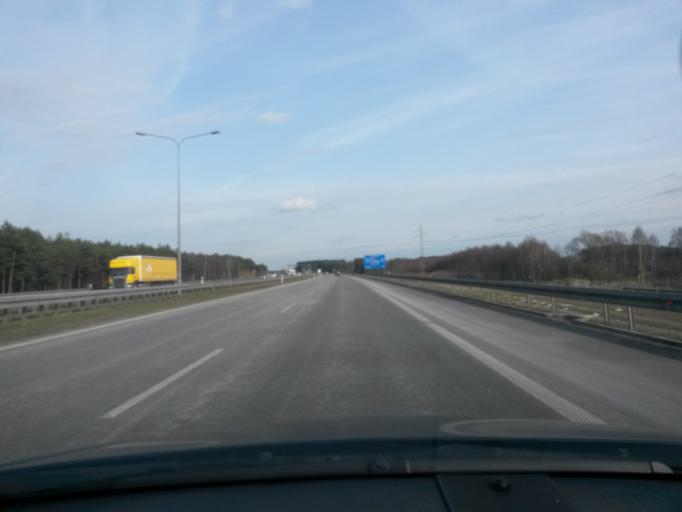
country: PL
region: Greater Poland Voivodeship
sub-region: Powiat koninski
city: Stare Miasto
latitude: 52.1507
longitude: 18.2838
